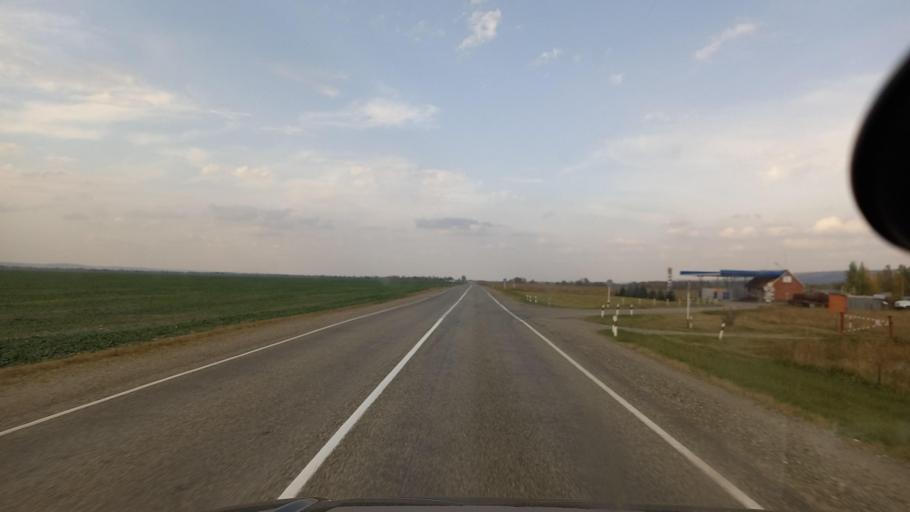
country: RU
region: Krasnodarskiy
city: Perepravnaya
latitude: 44.3317
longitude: 40.8480
